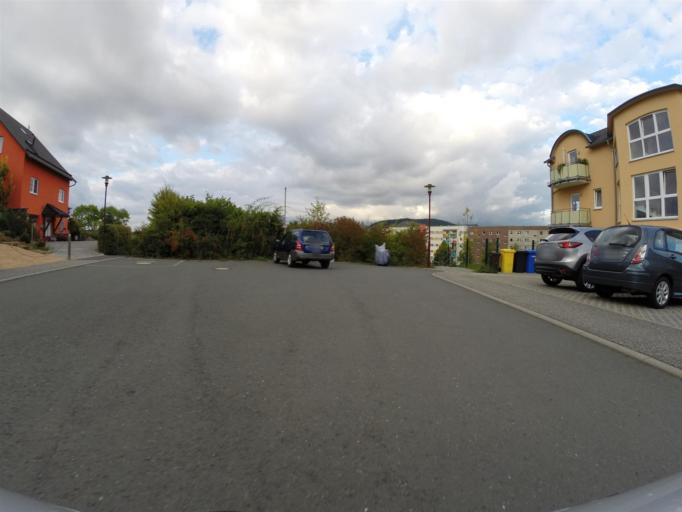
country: DE
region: Thuringia
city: Jena
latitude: 50.9017
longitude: 11.5693
